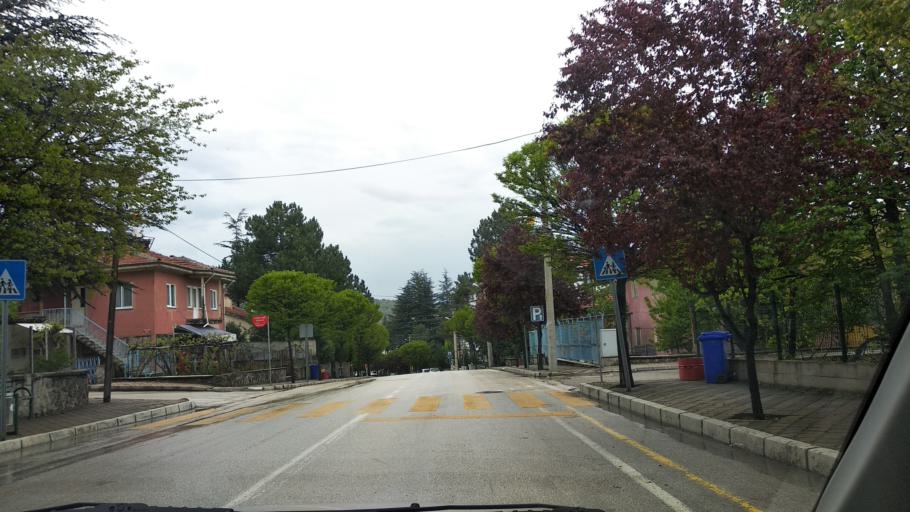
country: TR
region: Bolu
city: Seben
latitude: 40.4119
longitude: 31.5737
